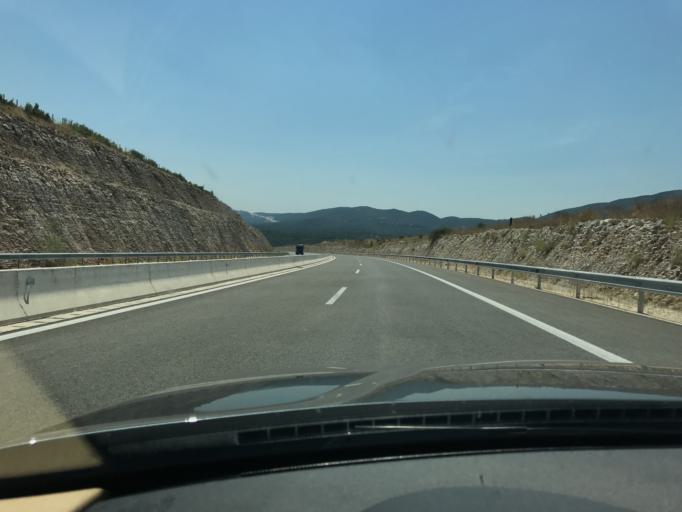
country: GR
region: Epirus
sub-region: Nomos Ioanninon
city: Agia Kyriaki
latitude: 39.4596
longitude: 20.8968
